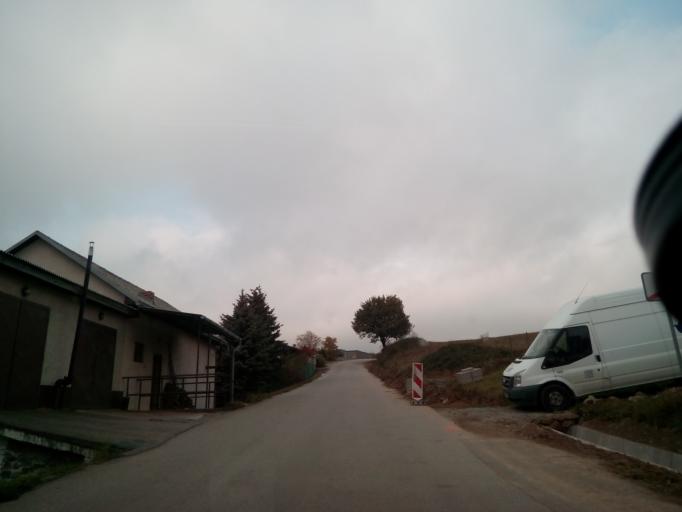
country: SK
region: Kosicky
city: Kosice
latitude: 48.7288
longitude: 21.1372
